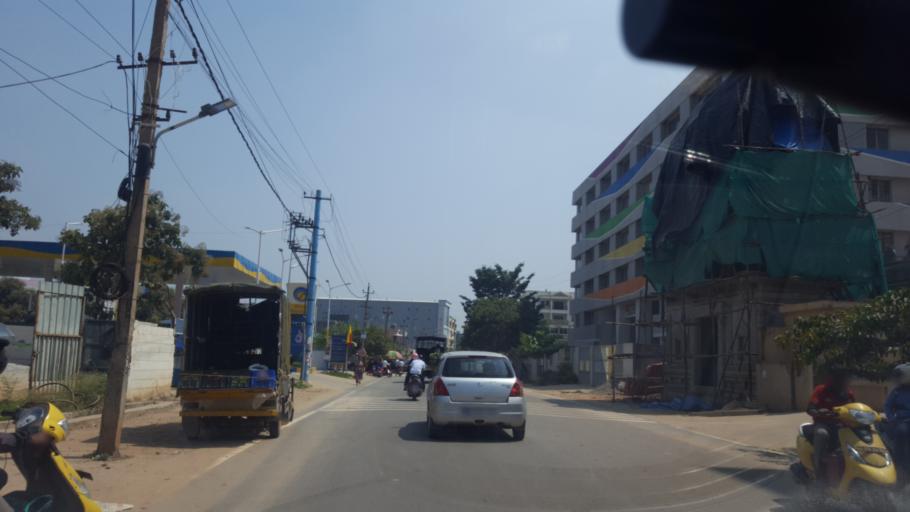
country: IN
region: Karnataka
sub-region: Bangalore Urban
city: Bangalore
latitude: 12.9380
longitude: 77.6997
